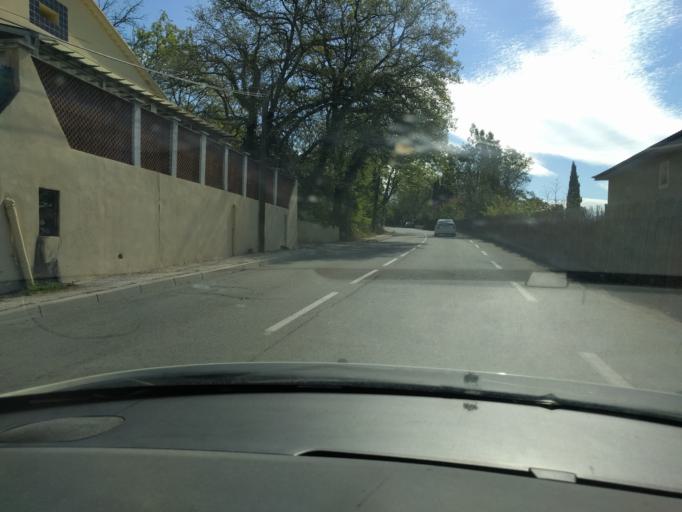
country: FR
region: Provence-Alpes-Cote d'Azur
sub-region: Departement du Var
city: Pierrefeu-du-Var
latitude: 43.2255
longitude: 6.1359
